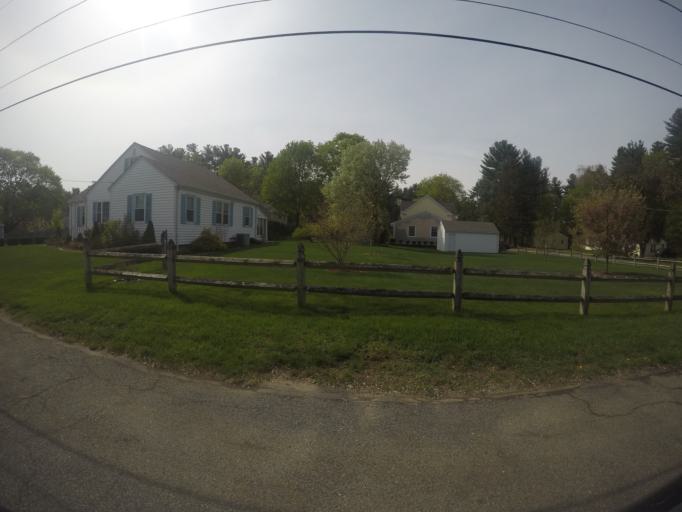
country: US
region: Massachusetts
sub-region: Bristol County
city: Easton
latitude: 42.0620
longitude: -71.0971
